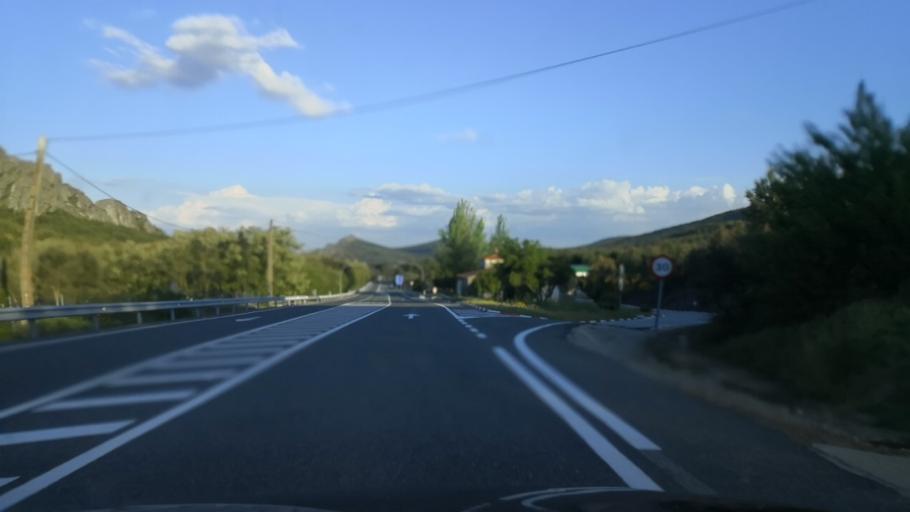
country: PT
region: Portalegre
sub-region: Portalegre
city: Sao Juliao
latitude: 39.3508
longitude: -7.3055
